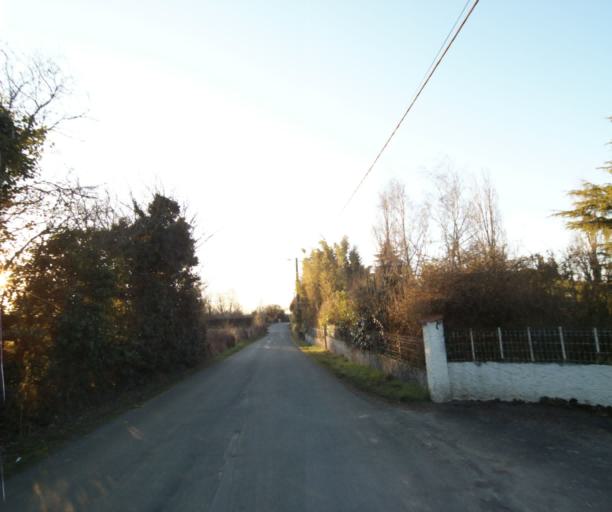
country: FR
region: Poitou-Charentes
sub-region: Departement des Deux-Sevres
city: Niort
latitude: 46.3541
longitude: -0.4432
